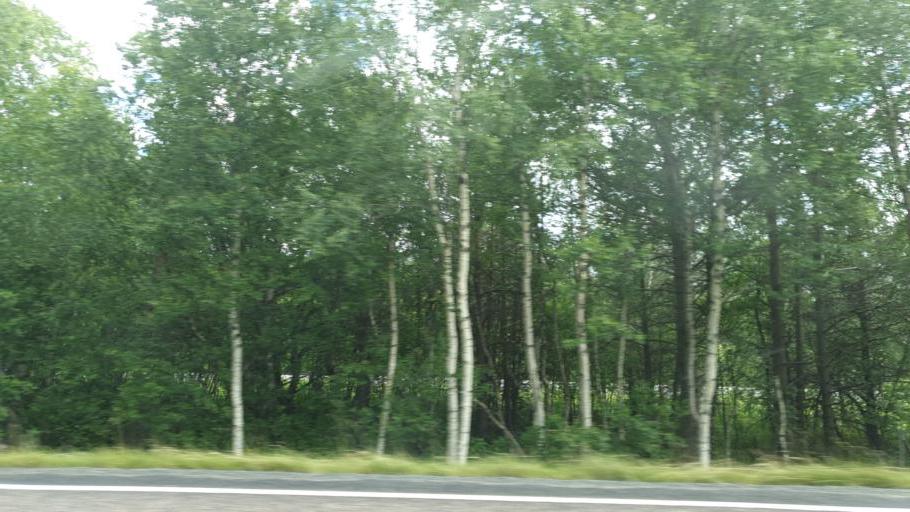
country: NO
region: Sor-Trondelag
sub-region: Oppdal
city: Oppdal
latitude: 62.6190
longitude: 9.7603
